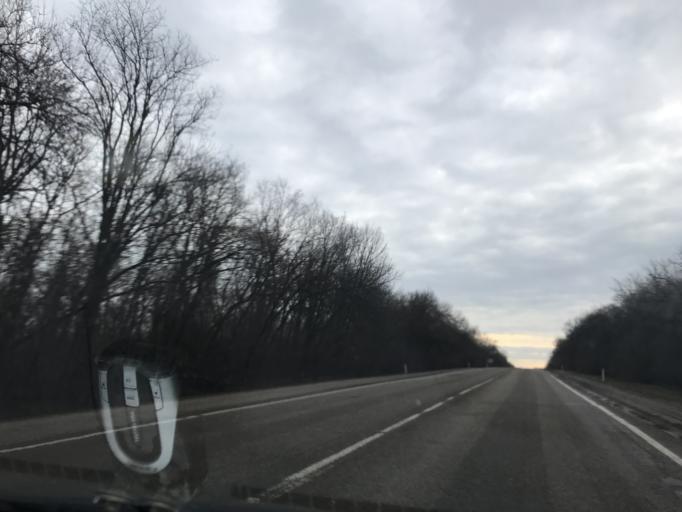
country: RU
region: Krasnodarskiy
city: Mirskoy
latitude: 45.5775
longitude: 40.4156
